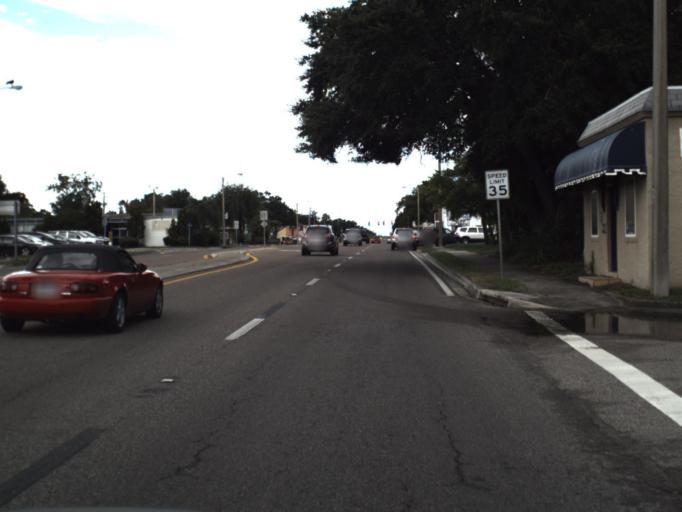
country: US
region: Florida
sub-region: Polk County
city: Mulberry
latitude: 27.8958
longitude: -81.9736
